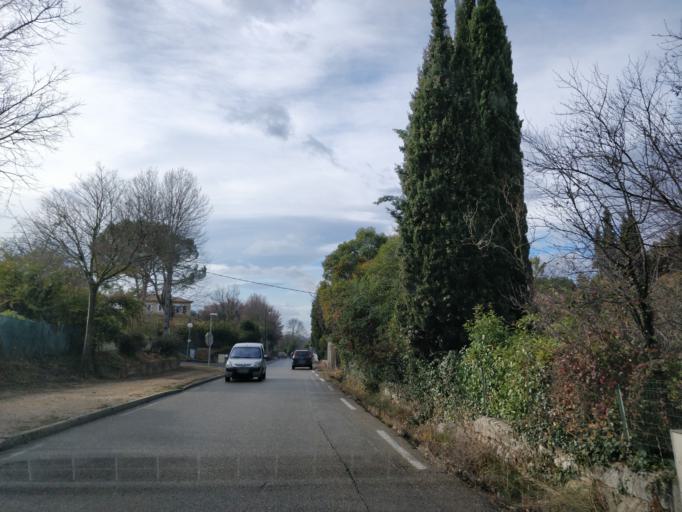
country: FR
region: Languedoc-Roussillon
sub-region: Departement du Gard
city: Villevieille
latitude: 43.7943
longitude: 4.0936
